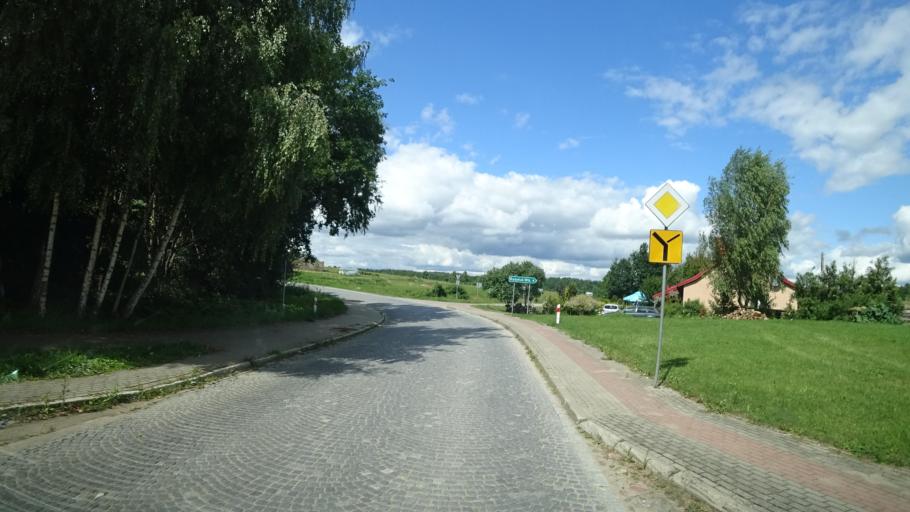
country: PL
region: Warmian-Masurian Voivodeship
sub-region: Powiat goldapski
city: Banie Mazurskie
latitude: 54.2193
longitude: 22.1521
